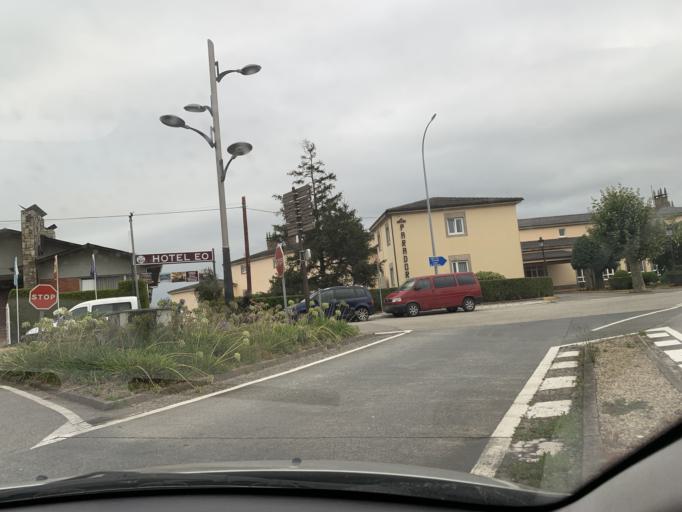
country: ES
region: Galicia
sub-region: Provincia de Lugo
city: Ribadeo
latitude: 43.5336
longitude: -7.0406
